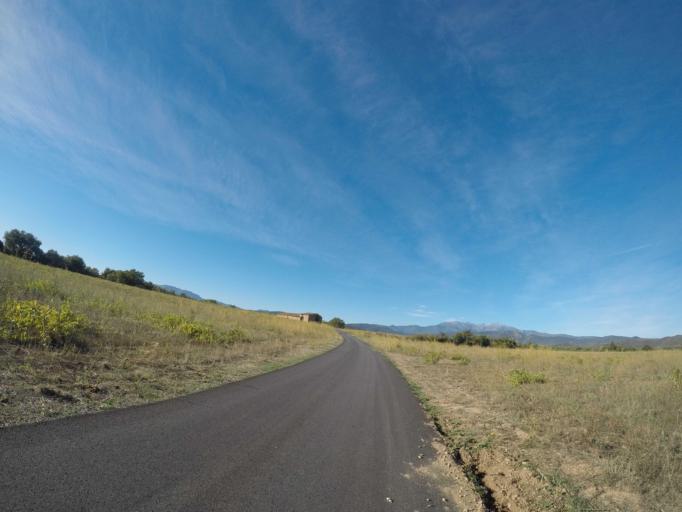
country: FR
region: Languedoc-Roussillon
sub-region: Departement des Pyrenees-Orientales
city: Llupia
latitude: 42.6013
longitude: 2.7671
